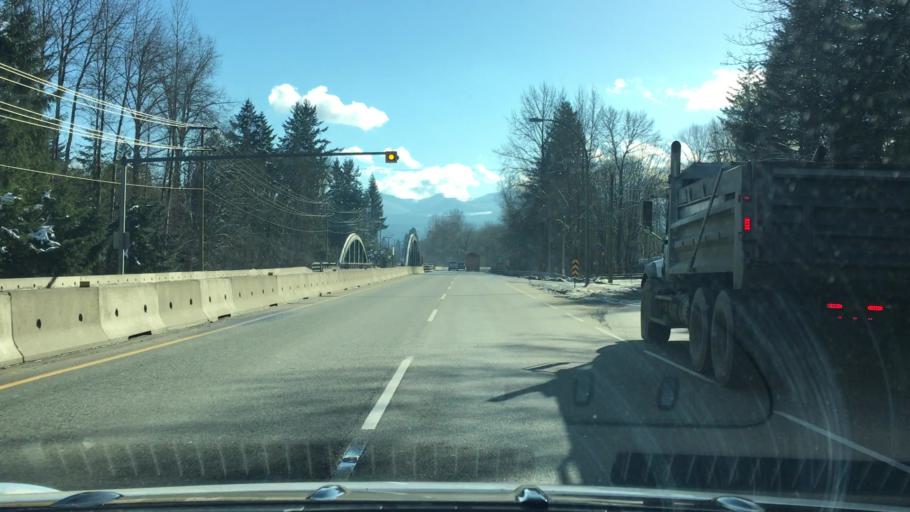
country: CA
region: British Columbia
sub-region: Cowichan Valley Regional District
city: Ladysmith
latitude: 49.0634
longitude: -123.8772
